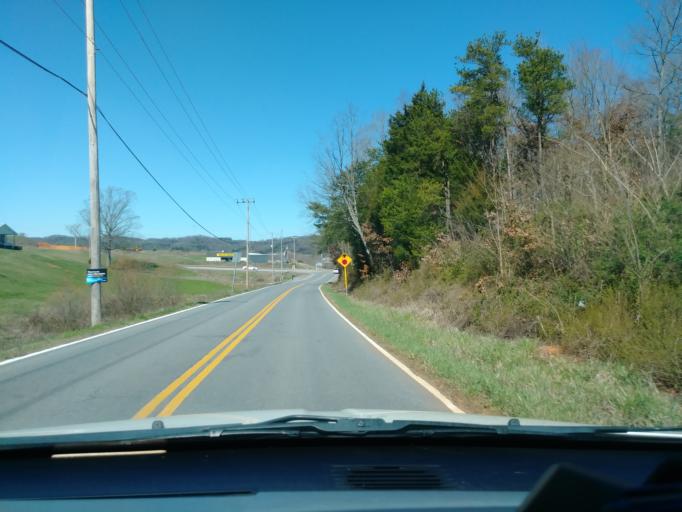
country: US
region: Tennessee
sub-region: Cocke County
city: Newport
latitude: 36.0027
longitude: -83.0896
